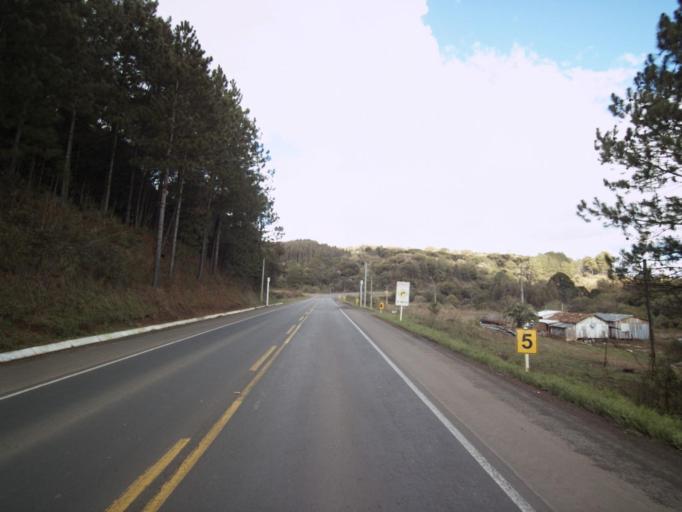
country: BR
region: Santa Catarina
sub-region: Joacaba
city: Joacaba
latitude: -27.0080
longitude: -51.7367
